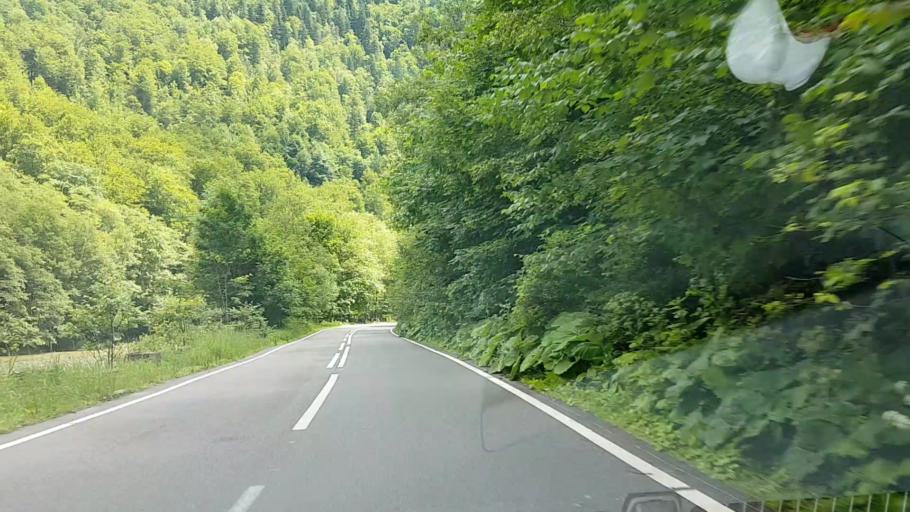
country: RO
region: Suceava
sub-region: Comuna Crucea
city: Crucea
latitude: 47.3125
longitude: 25.6281
